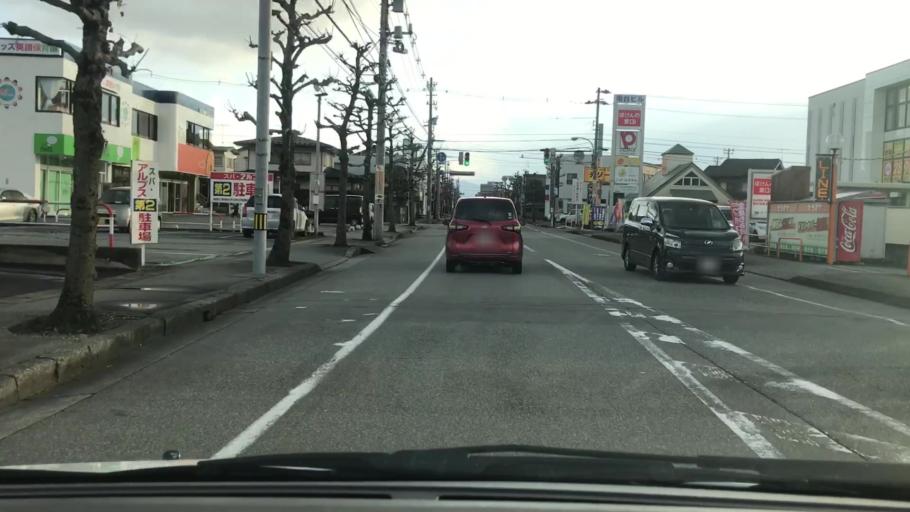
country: JP
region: Toyama
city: Toyama-shi
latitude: 36.6767
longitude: 137.2370
